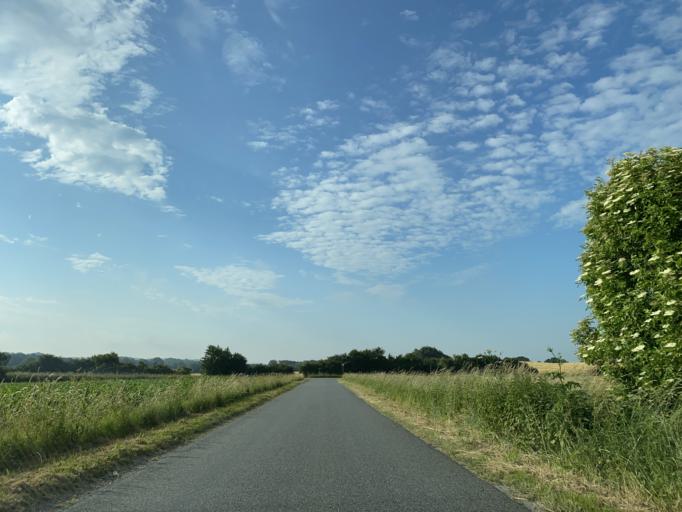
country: DK
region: South Denmark
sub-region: Haderslev Kommune
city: Haderslev
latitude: 55.1892
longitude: 9.4719
